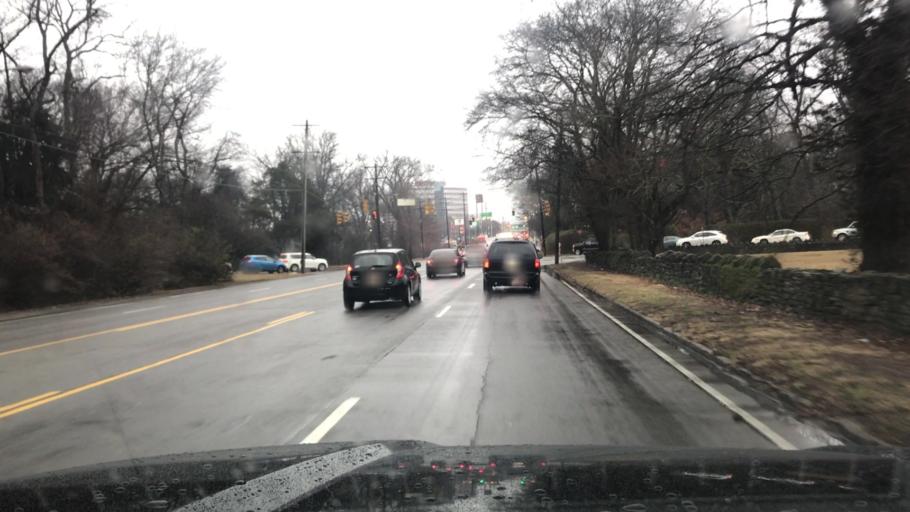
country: US
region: Tennessee
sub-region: Davidson County
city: Belle Meade
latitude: 36.1207
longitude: -86.8518
